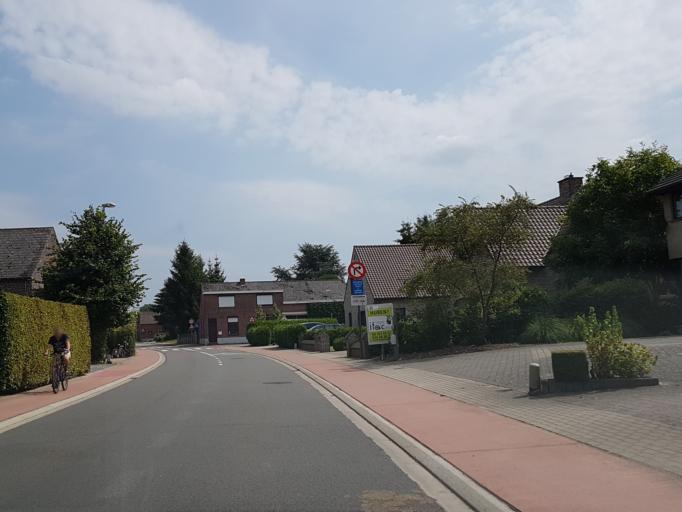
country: BE
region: Flanders
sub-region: Provincie Vlaams-Brabant
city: Herent
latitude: 50.9229
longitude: 4.6322
